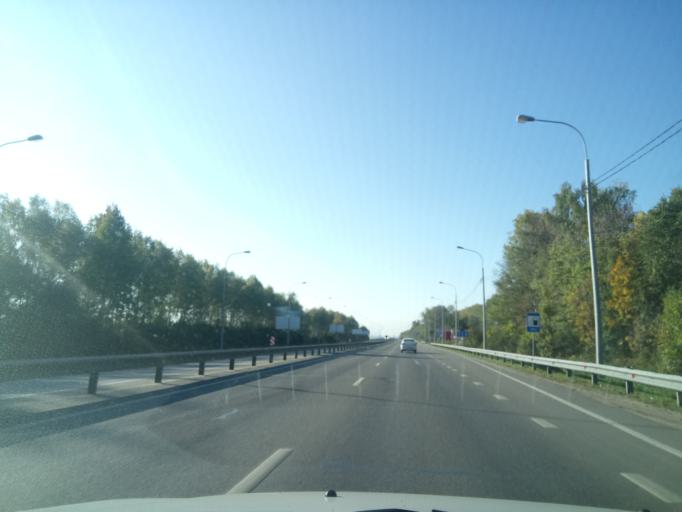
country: RU
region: Nizjnij Novgorod
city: Nizhniy Novgorod
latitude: 56.2108
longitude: 43.9283
